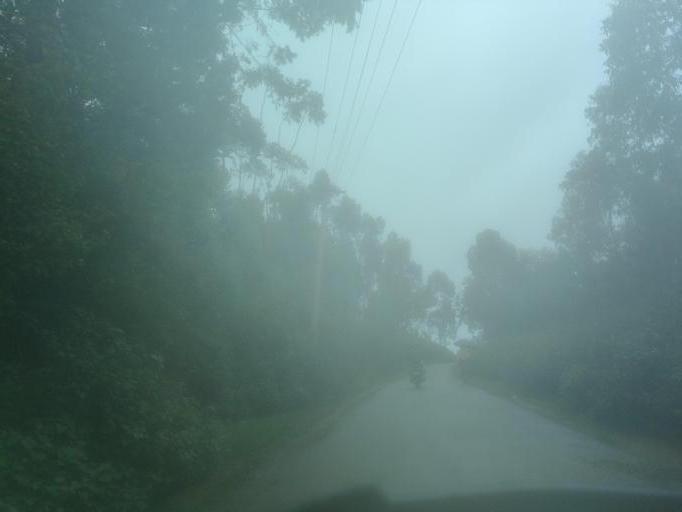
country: IN
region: Tamil Nadu
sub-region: Dindigul
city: Kodaikanal
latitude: 10.2043
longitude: 77.3449
